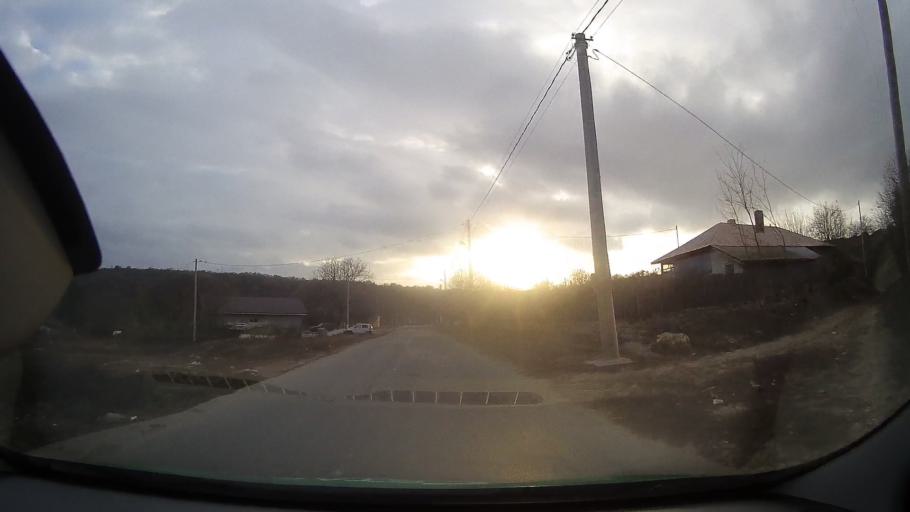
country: RO
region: Constanta
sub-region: Comuna Adamclisi
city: Adamclisi
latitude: 44.0415
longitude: 27.9540
